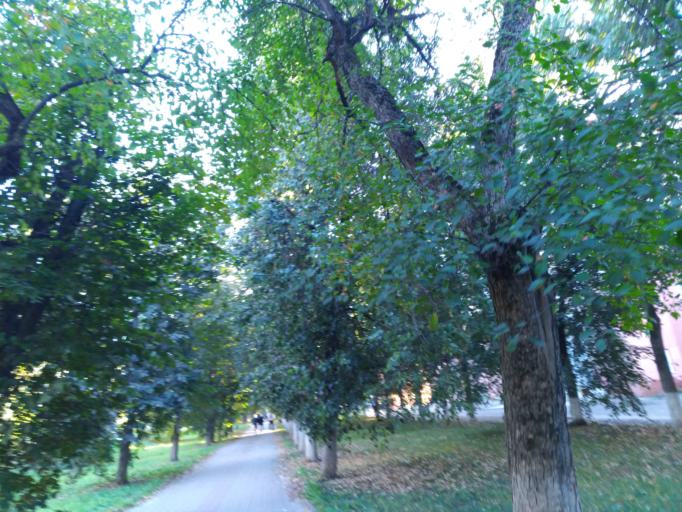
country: RU
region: Kaluga
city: Kaluga
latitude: 54.5323
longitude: 36.2761
